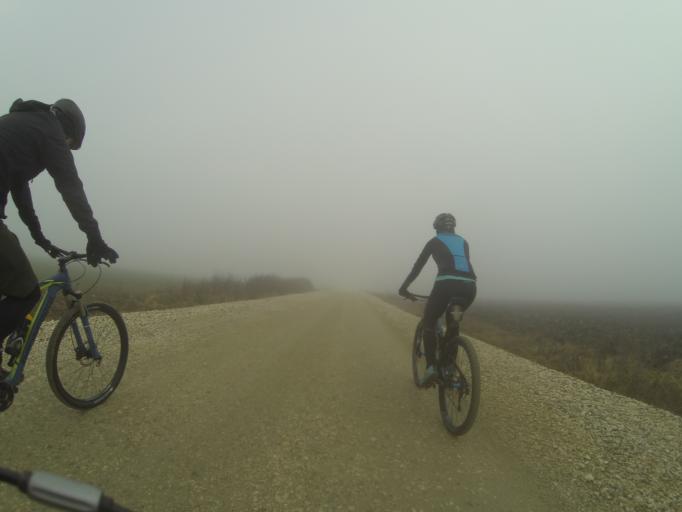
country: RO
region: Mehedinti
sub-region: Comuna Balacita
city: Gvardinita
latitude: 44.4327
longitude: 23.1333
